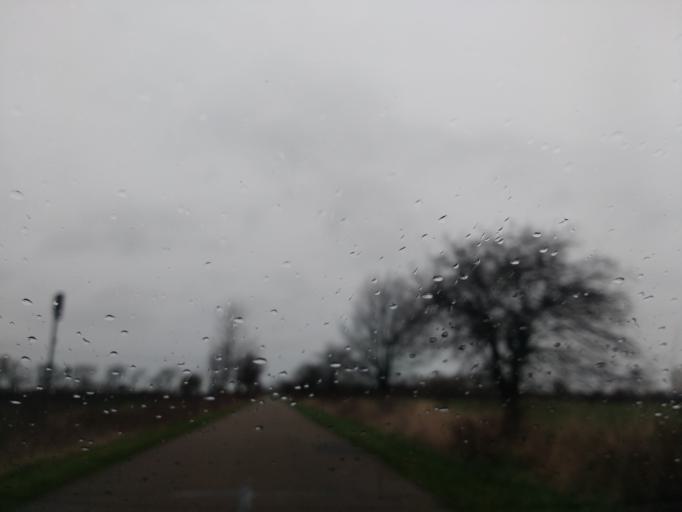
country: DE
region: Schleswig-Holstein
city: Grossenbrode
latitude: 54.3795
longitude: 11.0984
